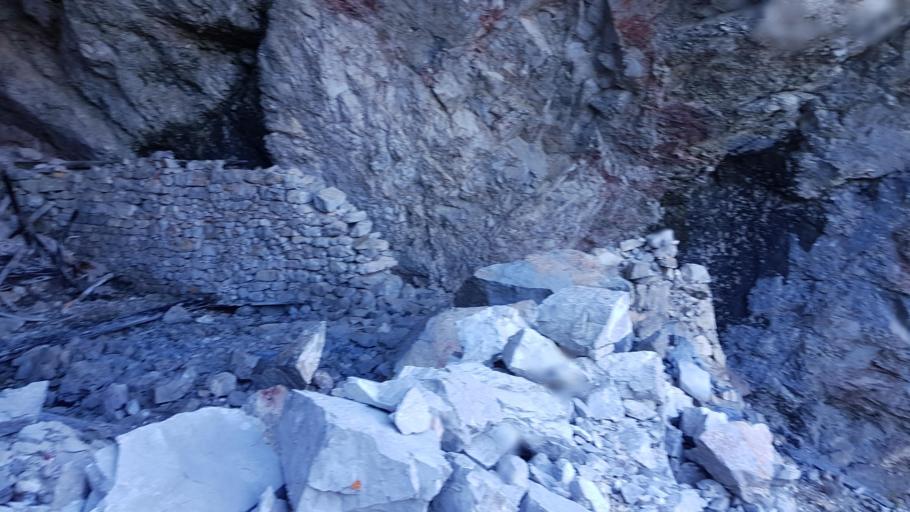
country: IT
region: Friuli Venezia Giulia
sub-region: Provincia di Udine
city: Malborghetto
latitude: 46.4699
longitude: 13.4155
